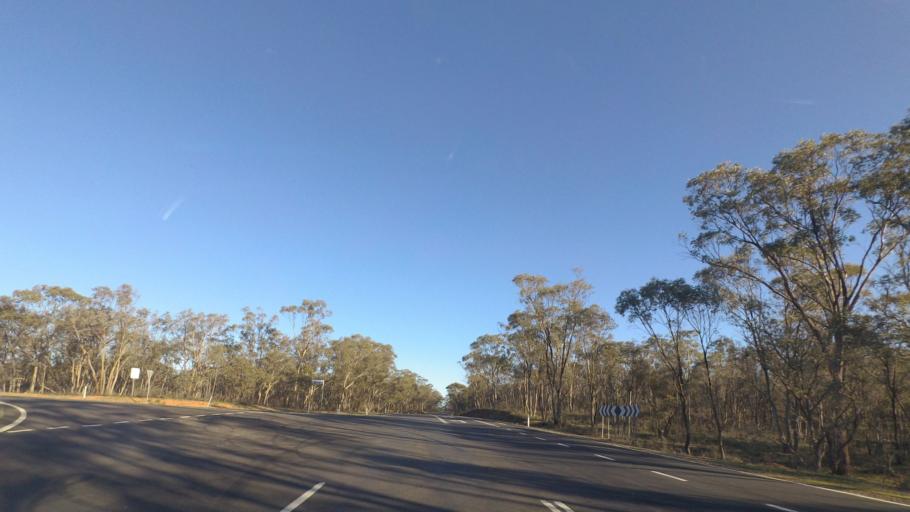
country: AU
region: Victoria
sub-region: Greater Bendigo
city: Kennington
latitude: -36.9096
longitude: 144.4932
